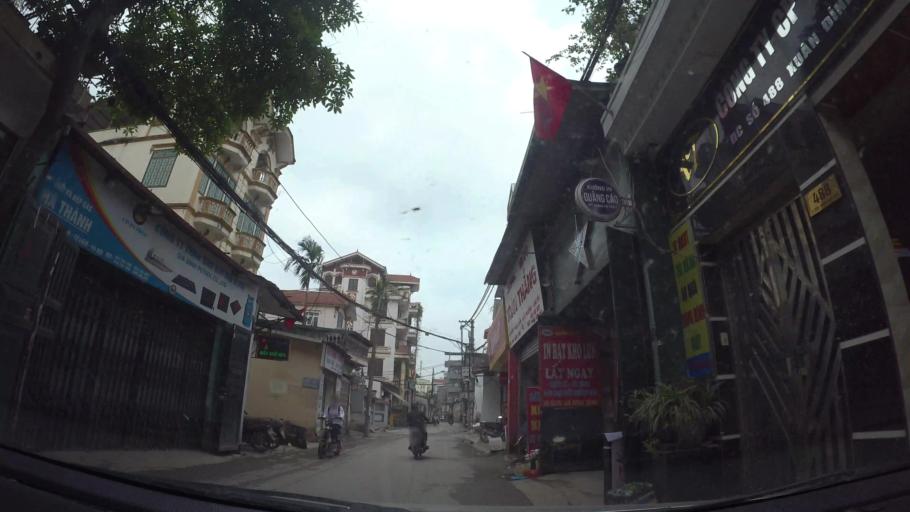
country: VN
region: Ha Noi
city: Tay Ho
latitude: 21.0743
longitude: 105.7887
